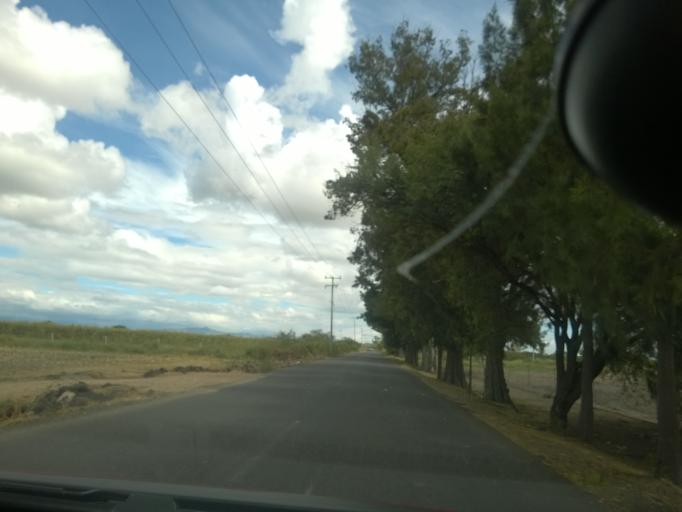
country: MX
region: Guanajuato
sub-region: Leon
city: El CERESO
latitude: 20.9923
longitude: -101.6591
